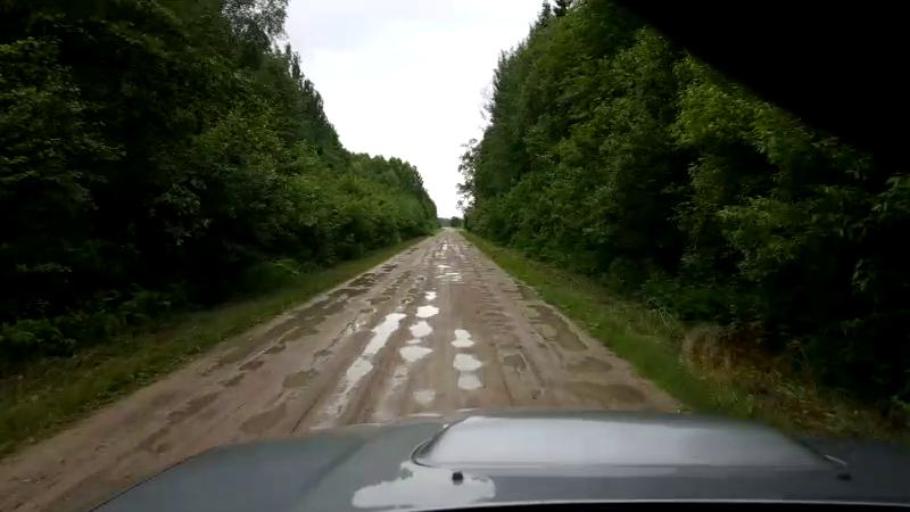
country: EE
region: Paernumaa
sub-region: Halinga vald
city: Parnu-Jaagupi
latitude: 58.5467
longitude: 24.5773
